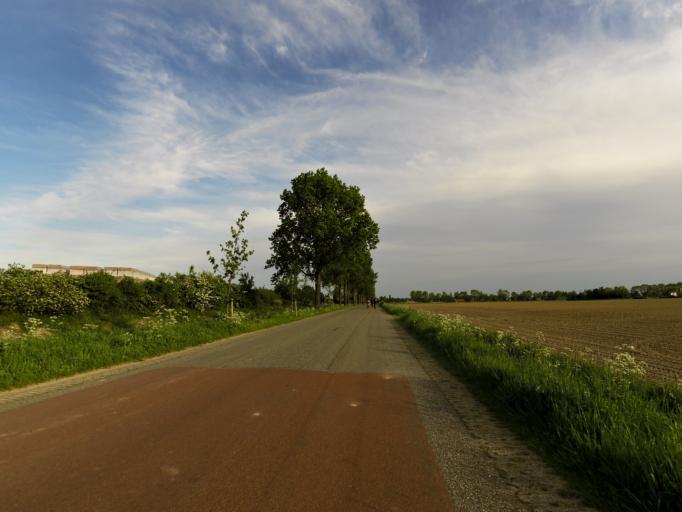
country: NL
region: Gelderland
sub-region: Gemeente Montferland
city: s-Heerenberg
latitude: 51.8964
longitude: 6.3048
